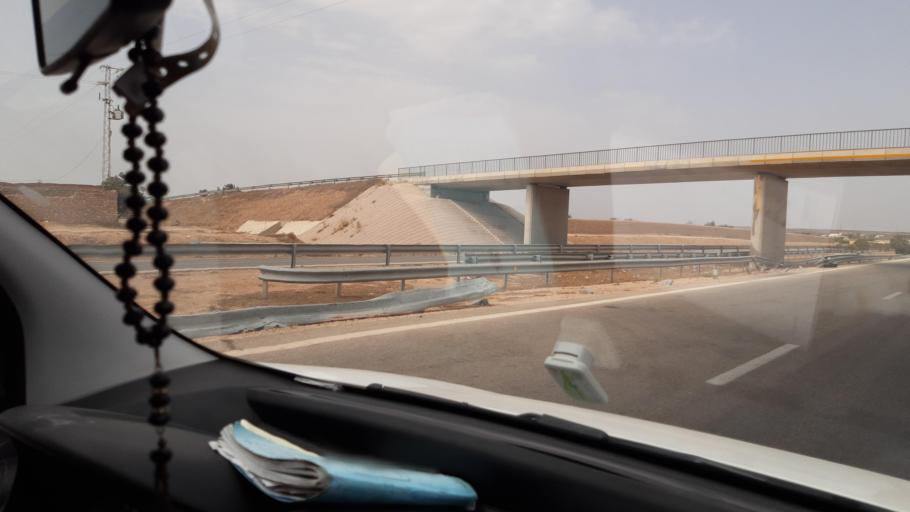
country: TN
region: Safaqis
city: Sfax
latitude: 34.8738
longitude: 10.6963
